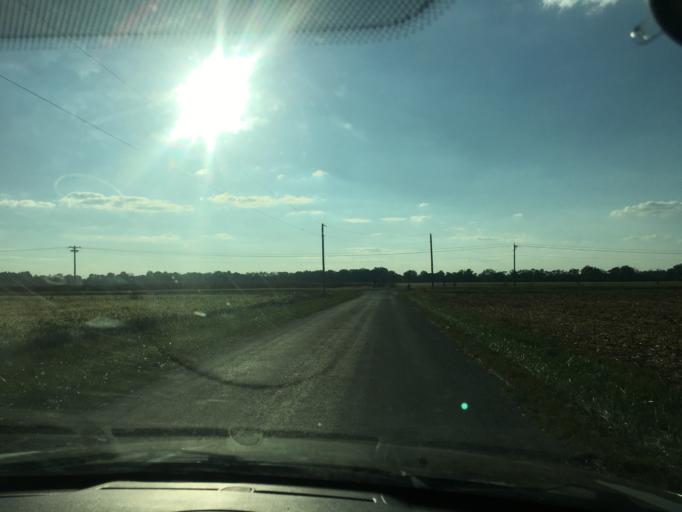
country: US
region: Ohio
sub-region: Champaign County
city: Urbana
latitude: 40.1721
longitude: -83.7819
